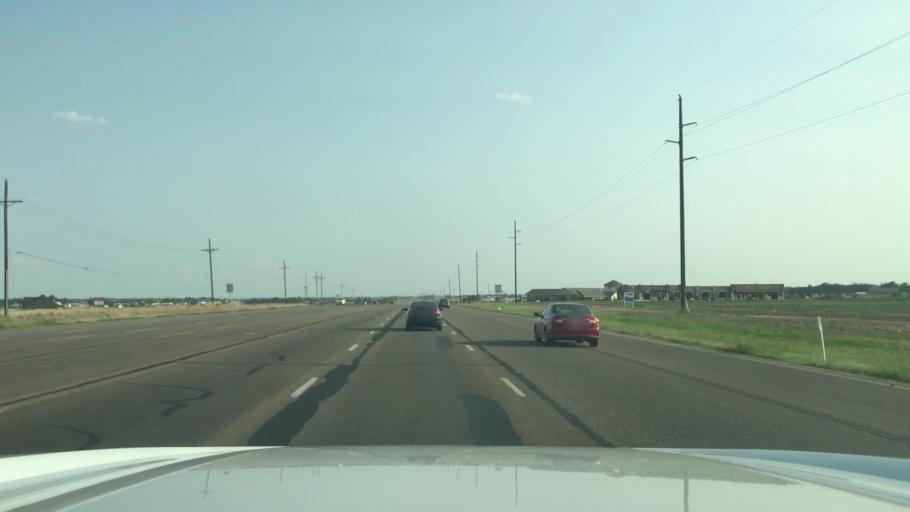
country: US
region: Texas
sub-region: Potter County
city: Amarillo
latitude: 35.1438
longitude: -101.9382
